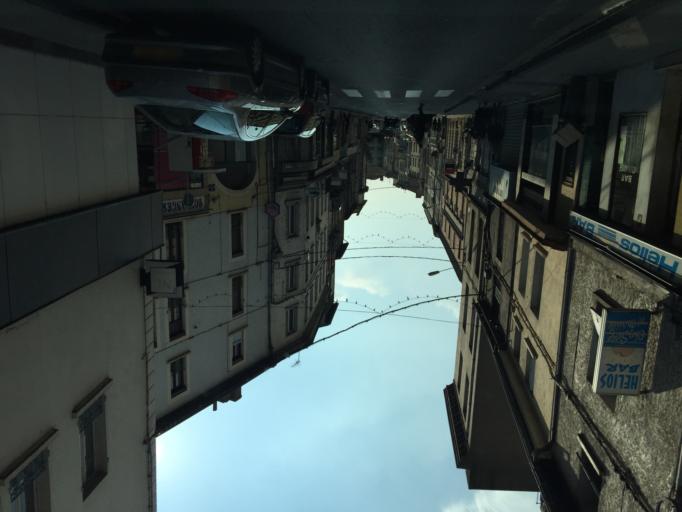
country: FR
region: Rhone-Alpes
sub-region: Departement de la Loire
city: Rive-de-Gier
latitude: 45.5293
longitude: 4.6166
